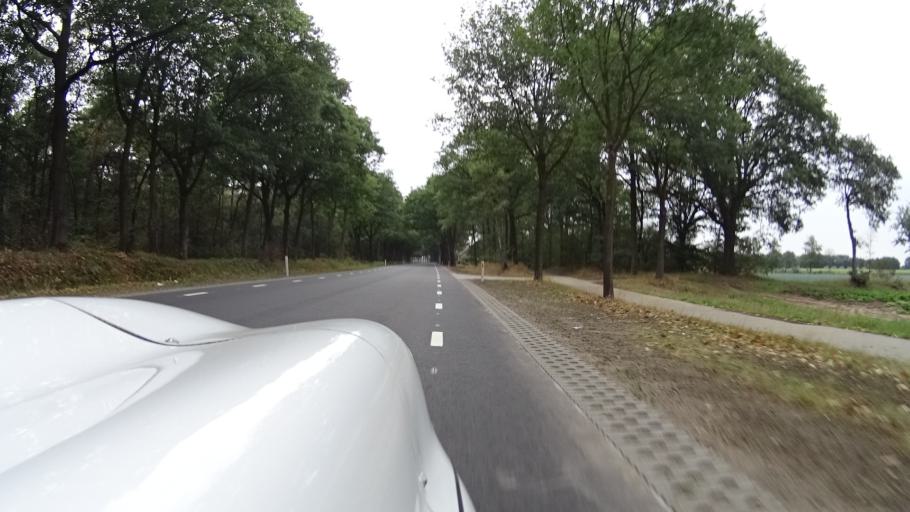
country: NL
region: North Brabant
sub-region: Gemeente Boekel
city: Boekel
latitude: 51.5800
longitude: 5.6461
